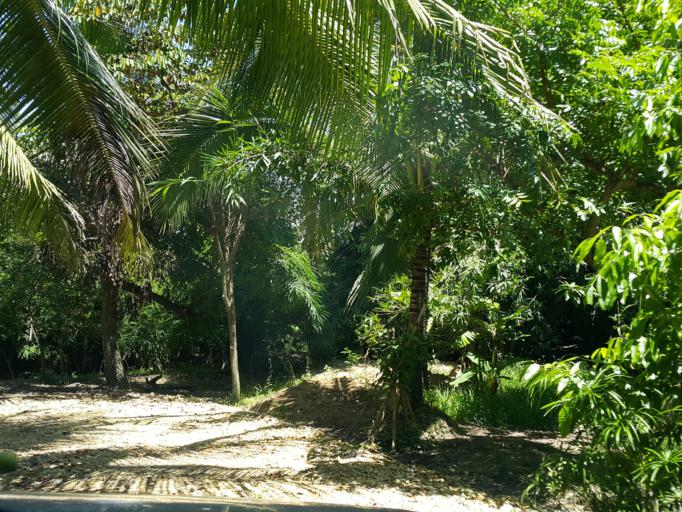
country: TH
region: Lamphun
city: Ban Thi
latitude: 18.6660
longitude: 99.1577
